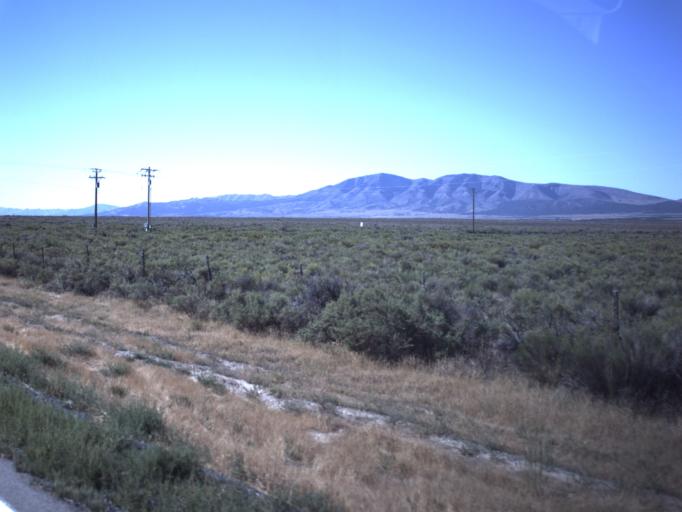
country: US
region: Utah
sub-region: Tooele County
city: Tooele
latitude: 40.3856
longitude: -112.3864
